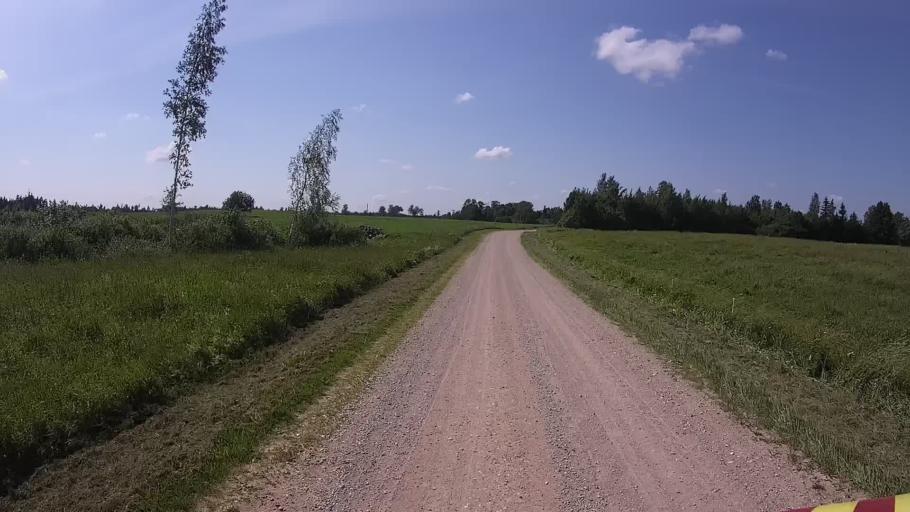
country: EE
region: Viljandimaa
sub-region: Karksi vald
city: Karksi-Nuia
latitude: 58.0041
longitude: 25.5162
